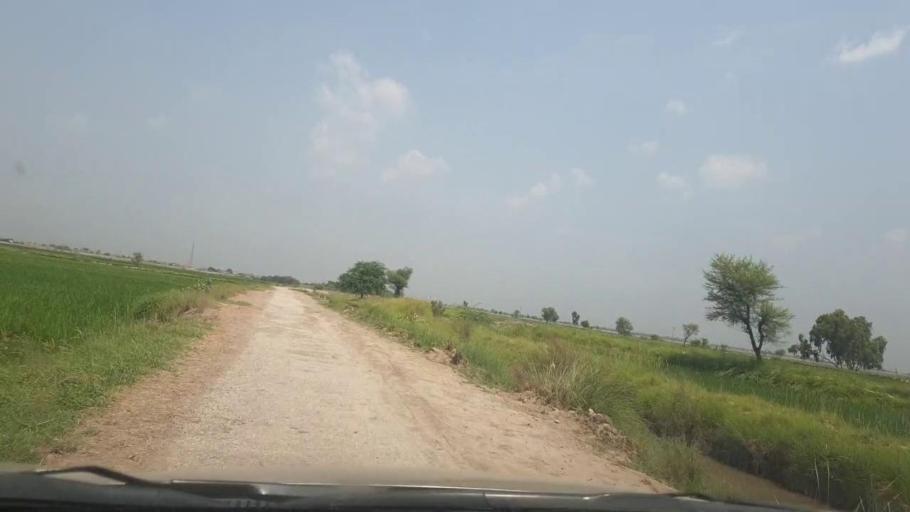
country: PK
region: Sindh
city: Ratodero
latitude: 27.6905
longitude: 68.2334
